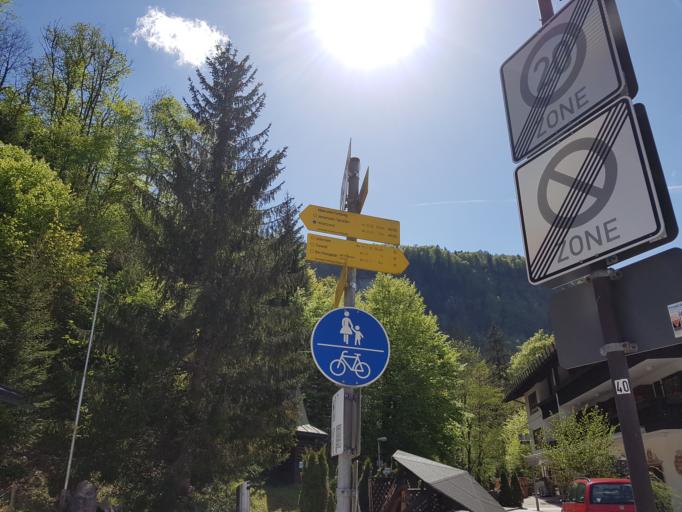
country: DE
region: Bavaria
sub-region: Upper Bavaria
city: Schoenau am Koenigssee
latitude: 47.5911
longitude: 12.9877
